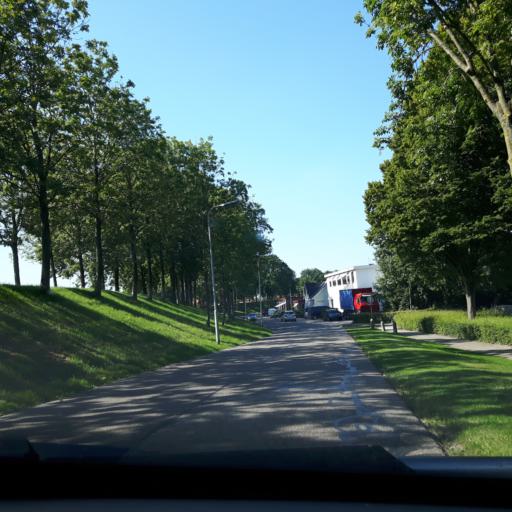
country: NL
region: Zeeland
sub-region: Gemeente Reimerswaal
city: Yerseke
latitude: 51.4972
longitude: 4.0485
